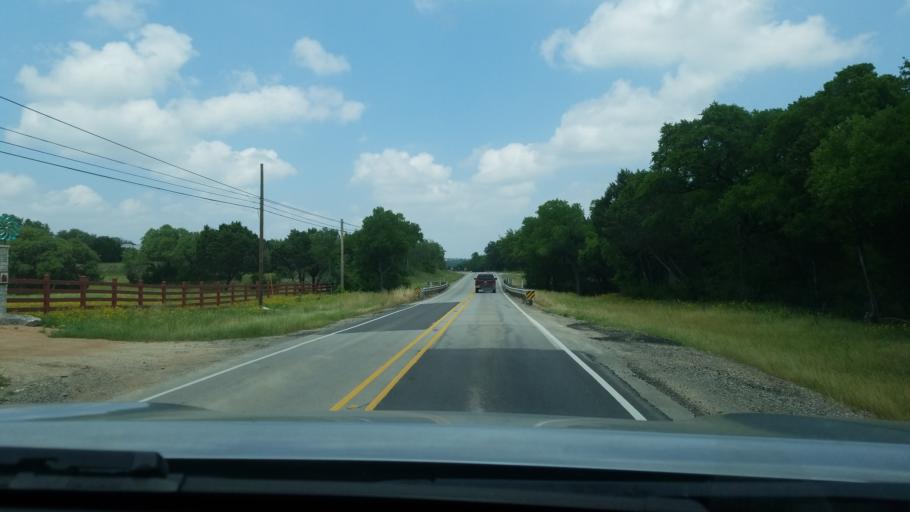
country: US
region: Texas
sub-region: Hays County
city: Dripping Springs
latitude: 30.1390
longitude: -98.0320
